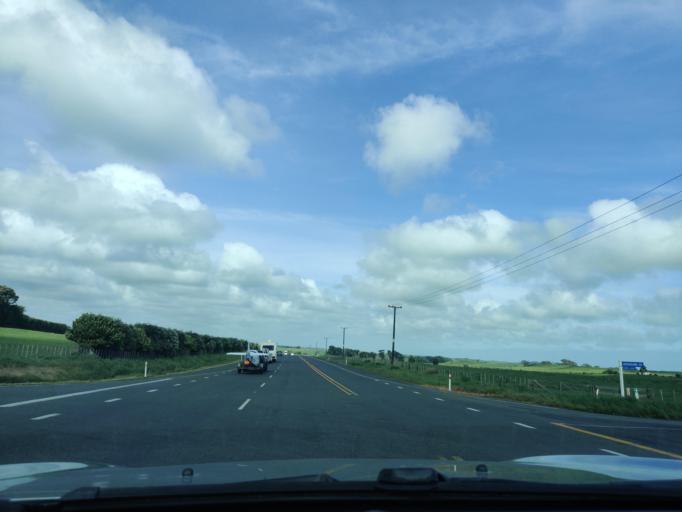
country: NZ
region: Taranaki
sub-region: South Taranaki District
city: Patea
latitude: -39.7665
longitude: 174.6513
